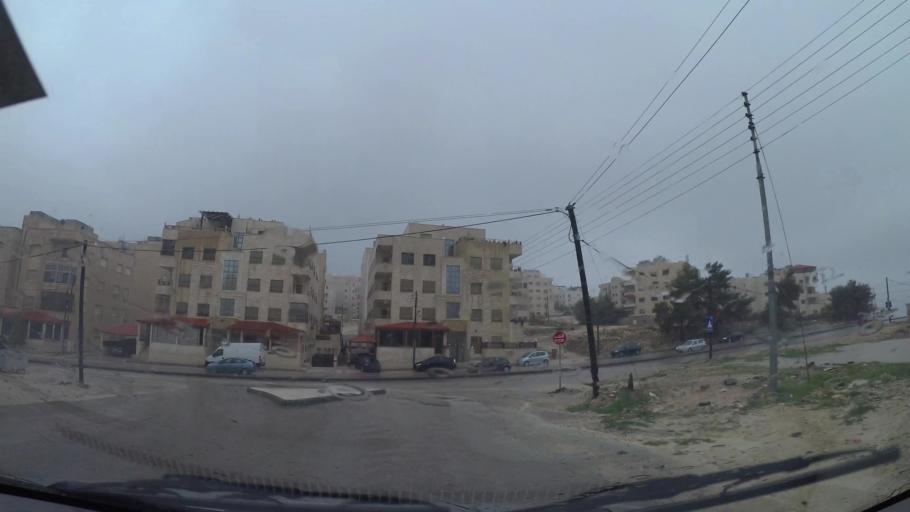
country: JO
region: Amman
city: Al Jubayhah
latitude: 32.0203
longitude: 35.8850
